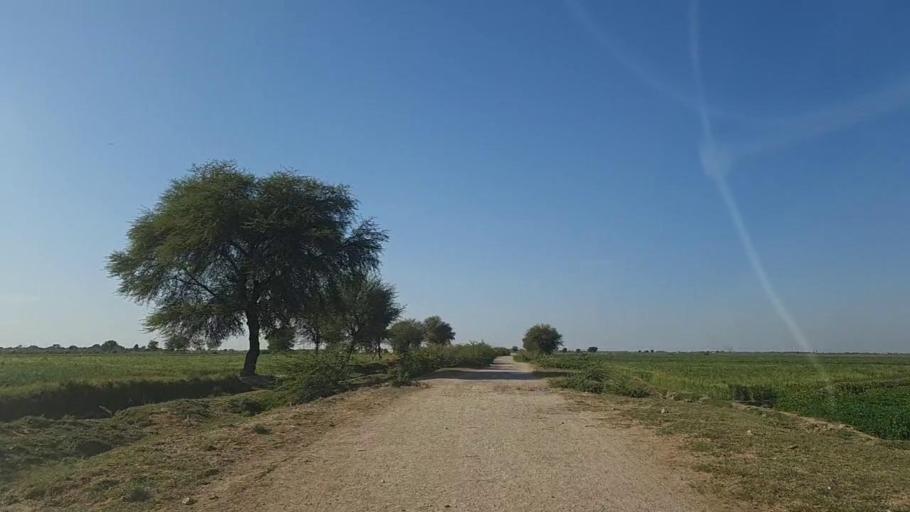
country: PK
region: Sindh
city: Kunri
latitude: 25.2288
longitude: 69.5076
